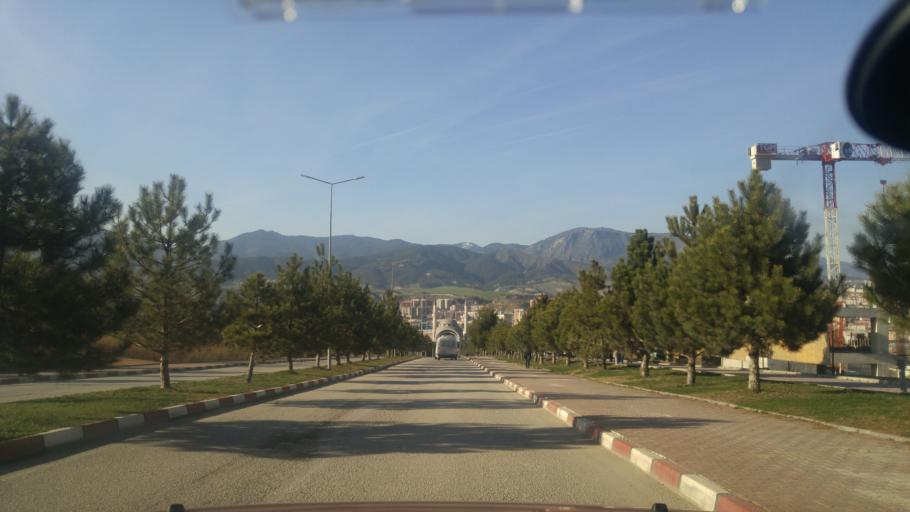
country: TR
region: Karabuk
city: Karabuk
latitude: 41.2067
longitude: 32.6580
